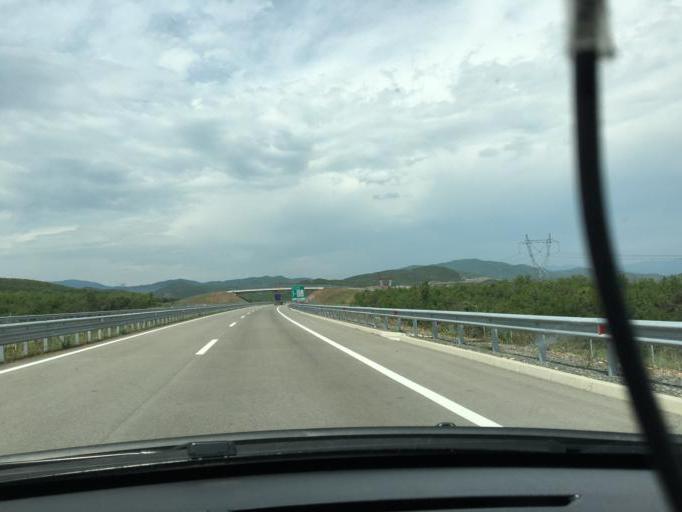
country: MK
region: Gevgelija
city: Miravci
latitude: 41.2853
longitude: 22.4427
